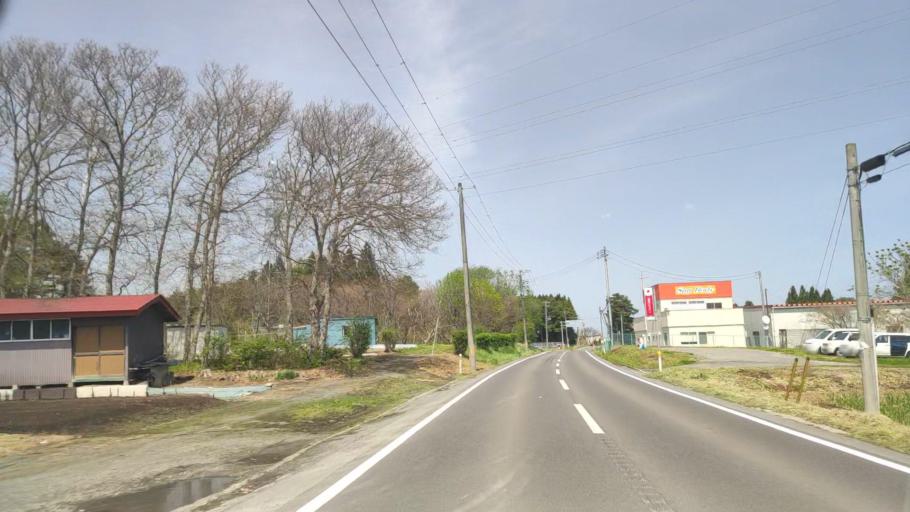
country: JP
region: Aomori
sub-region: Hachinohe Shi
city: Uchimaru
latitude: 40.5338
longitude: 141.4027
